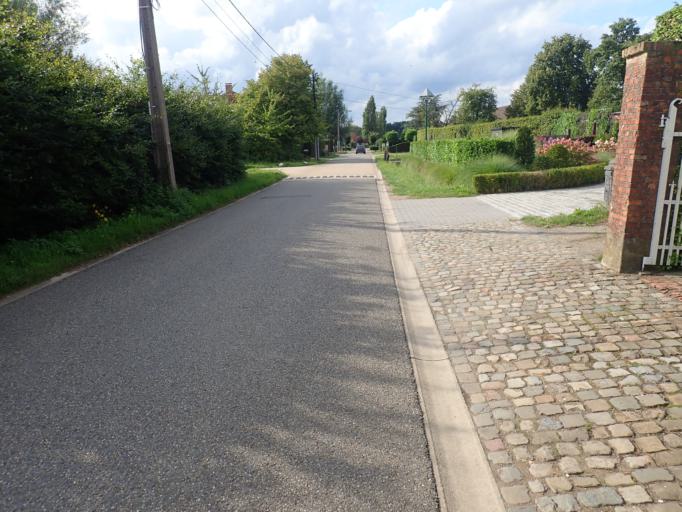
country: BE
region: Flanders
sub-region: Provincie Antwerpen
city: Zoersel
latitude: 51.2546
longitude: 4.7169
